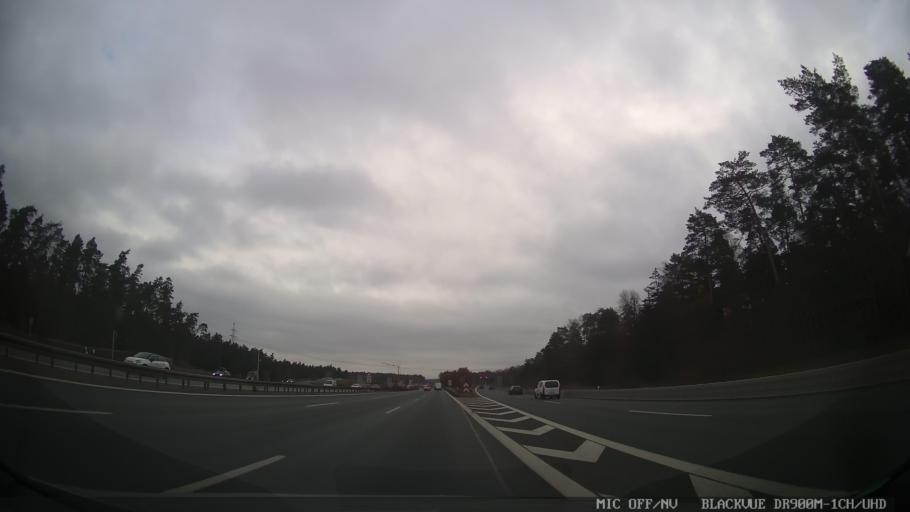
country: DE
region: Bavaria
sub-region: Regierungsbezirk Mittelfranken
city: Rothenbach an der Pegnitz
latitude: 49.4475
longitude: 11.2325
